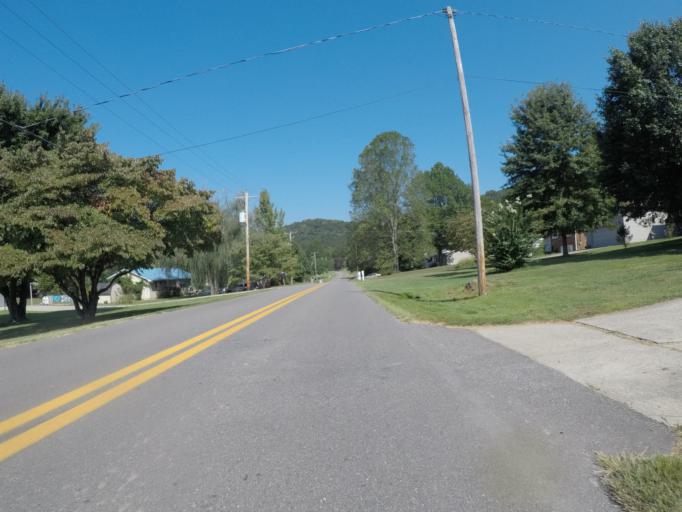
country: US
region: West Virginia
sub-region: Cabell County
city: Barboursville
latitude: 38.3728
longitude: -82.2751
